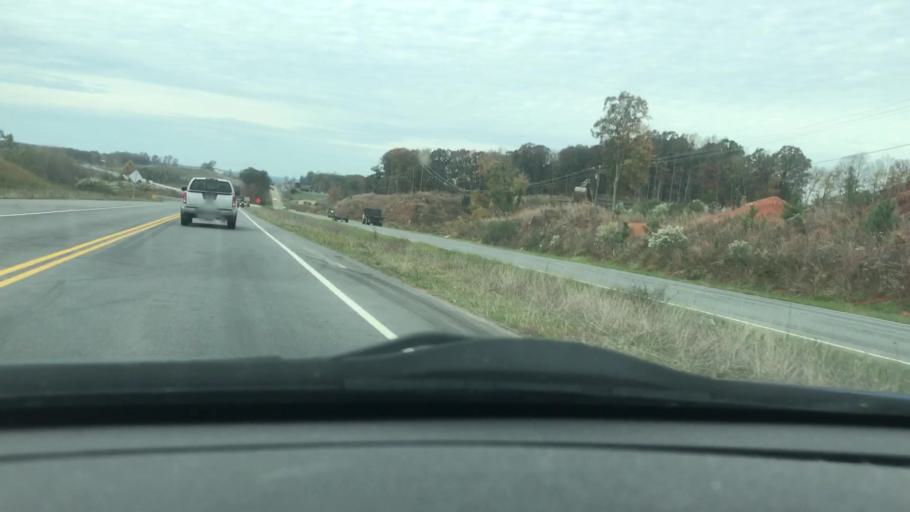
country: US
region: North Carolina
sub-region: Randolph County
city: Asheboro
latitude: 35.6949
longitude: -79.8602
